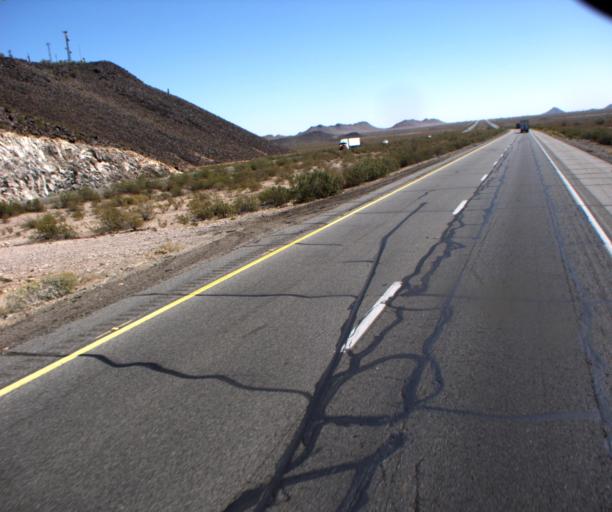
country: US
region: Arizona
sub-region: Maricopa County
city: Buckeye
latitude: 33.5283
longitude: -113.1154
